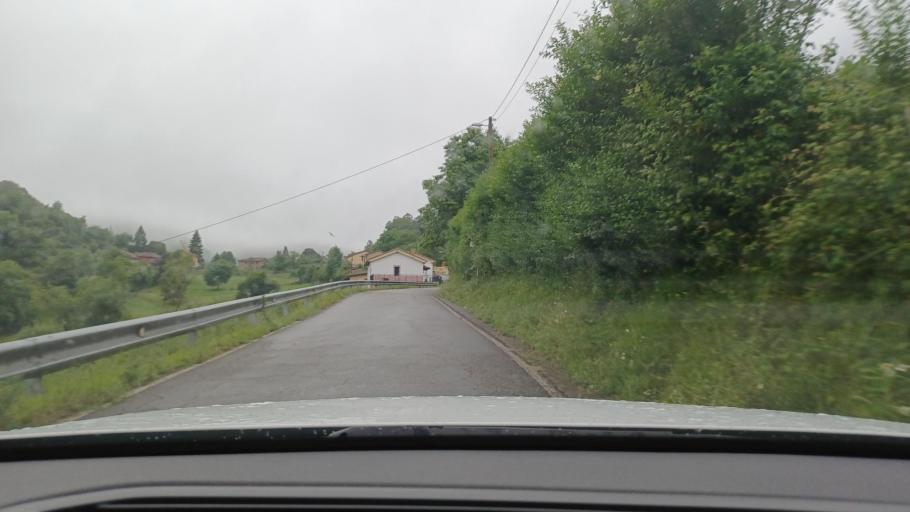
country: ES
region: Asturias
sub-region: Province of Asturias
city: Castandiello
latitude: 43.3051
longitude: -5.9325
